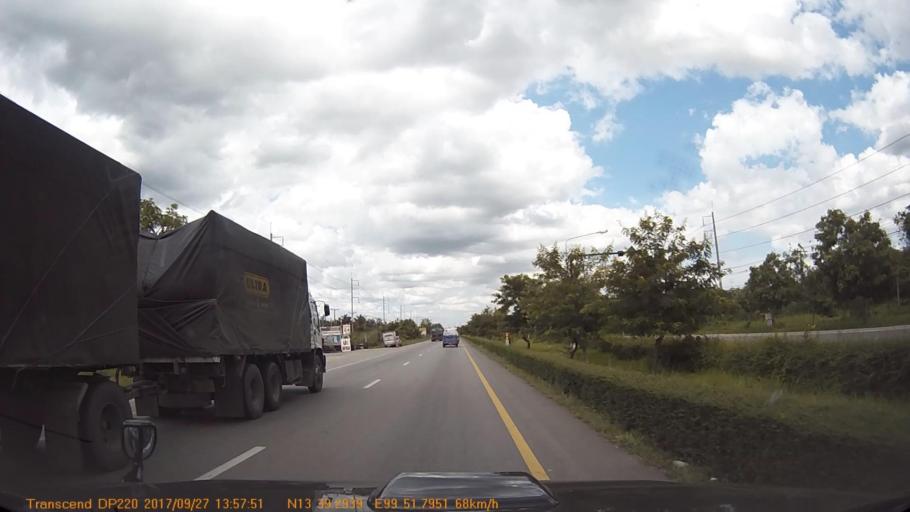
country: TH
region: Ratchaburi
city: Photharam
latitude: 13.6549
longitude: 99.8632
